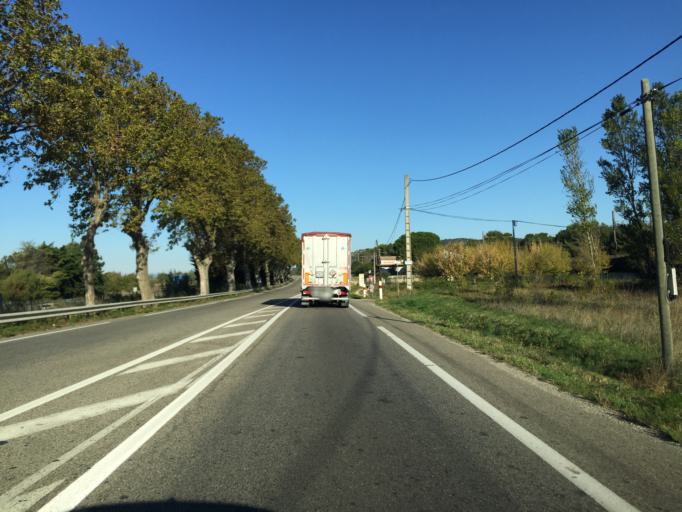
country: FR
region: Provence-Alpes-Cote d'Azur
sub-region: Departement du Vaucluse
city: Piolenc
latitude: 44.1865
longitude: 4.7492
